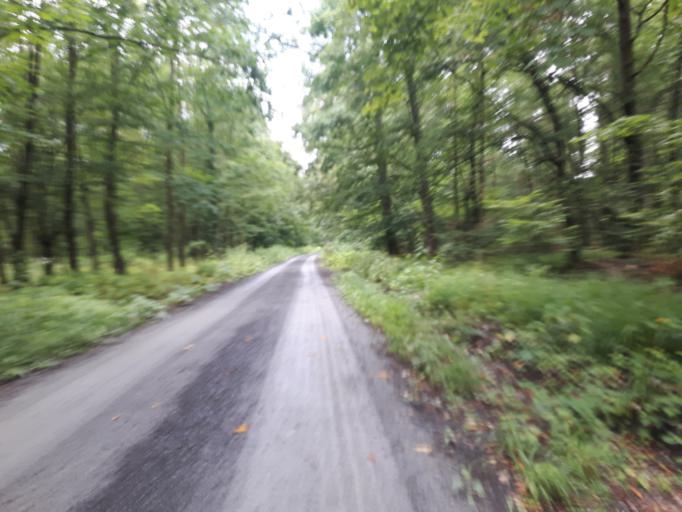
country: DE
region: Baden-Wuerttemberg
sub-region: Regierungsbezirk Stuttgart
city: Eppingen
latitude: 49.1134
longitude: 8.9407
